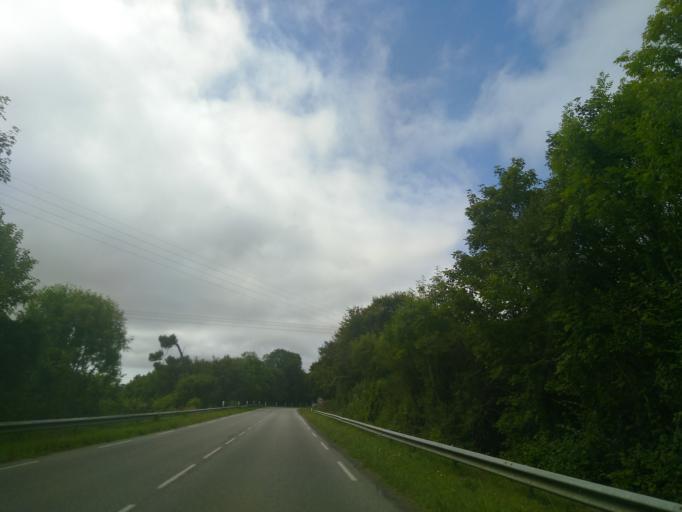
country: FR
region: Brittany
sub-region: Departement du Finistere
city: Audierne
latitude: 48.0392
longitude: -4.5274
